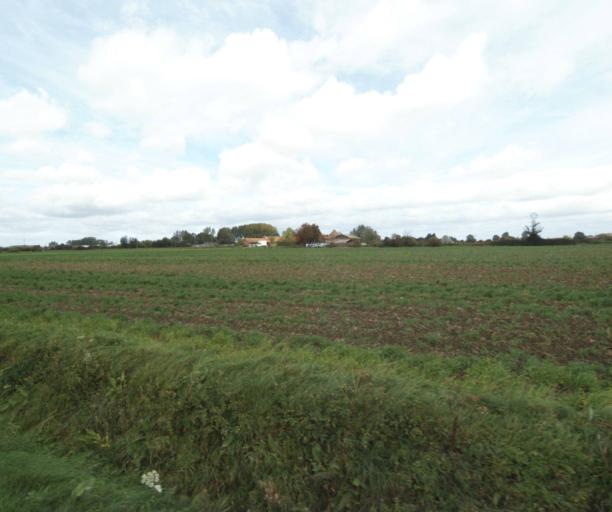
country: FR
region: Nord-Pas-de-Calais
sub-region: Departement du Nord
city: Houplines
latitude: 50.6708
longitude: 2.9260
